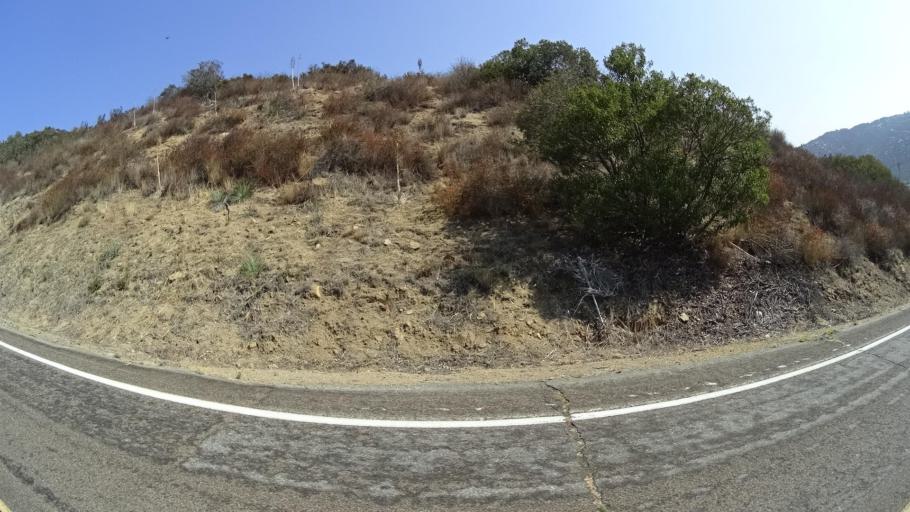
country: US
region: California
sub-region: San Diego County
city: Hidden Meadows
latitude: 33.2337
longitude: -117.1519
